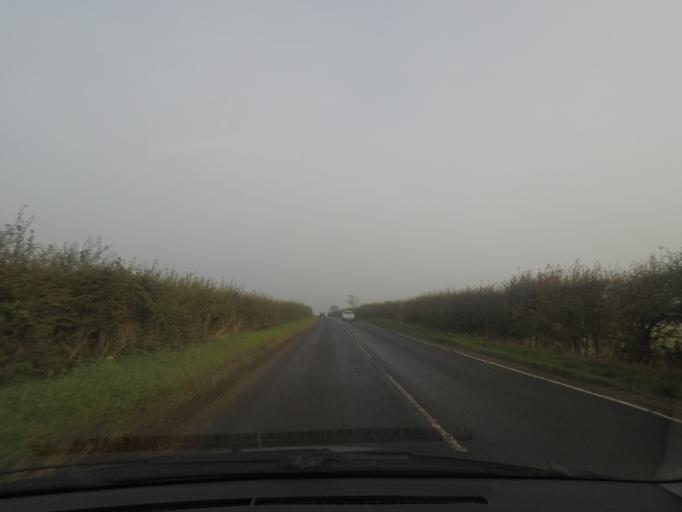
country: GB
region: England
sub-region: City and Borough of Leeds
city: Walton
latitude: 54.0124
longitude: -1.3091
